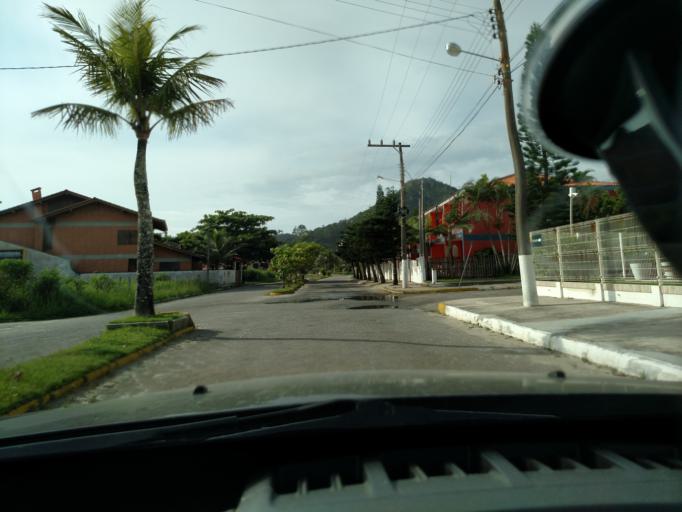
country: BR
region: Santa Catarina
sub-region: Porto Belo
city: Porto Belo
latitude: -27.1934
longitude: -48.4985
